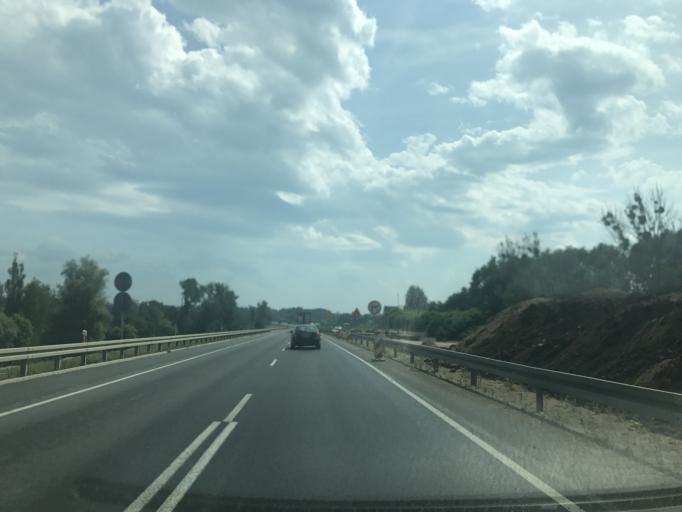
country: PL
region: Warmian-Masurian Voivodeship
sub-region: Powiat ostrodzki
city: Ostroda
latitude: 53.6995
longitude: 19.9807
